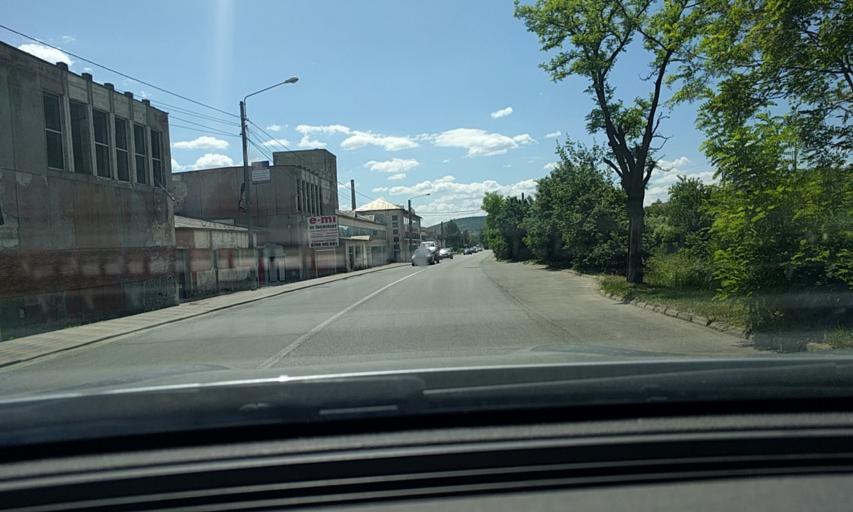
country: RO
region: Bistrita-Nasaud
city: Bistrita
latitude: 47.1375
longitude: 24.4794
